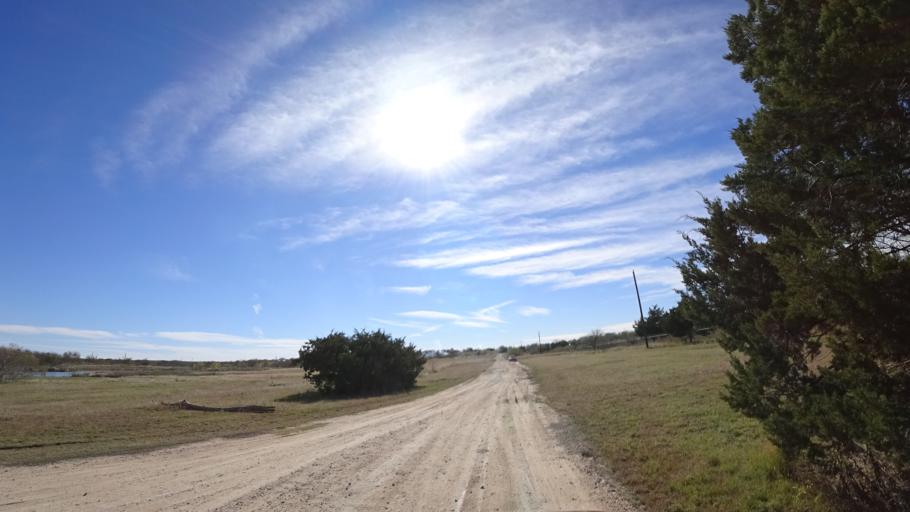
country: US
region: Texas
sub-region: Travis County
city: Onion Creek
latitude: 30.1129
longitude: -97.7155
